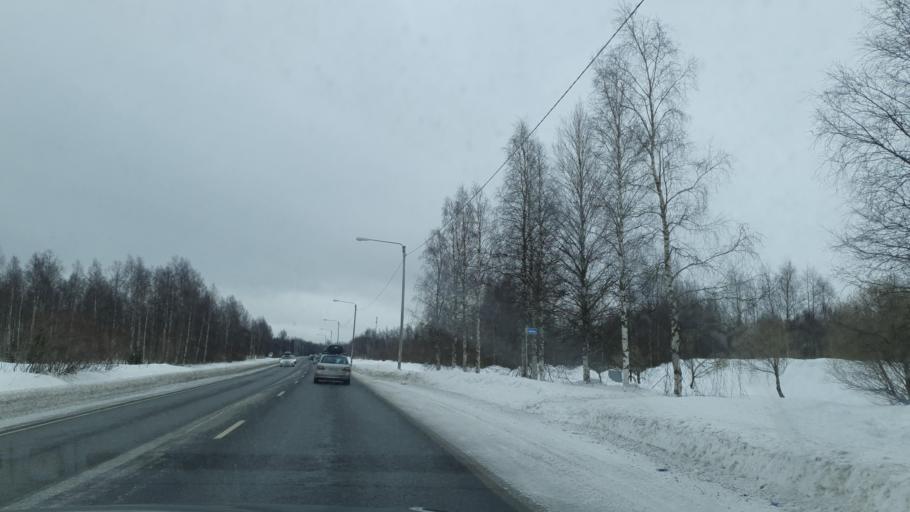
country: FI
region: Lapland
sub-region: Kemi-Tornio
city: Tornio
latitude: 65.8781
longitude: 24.1561
